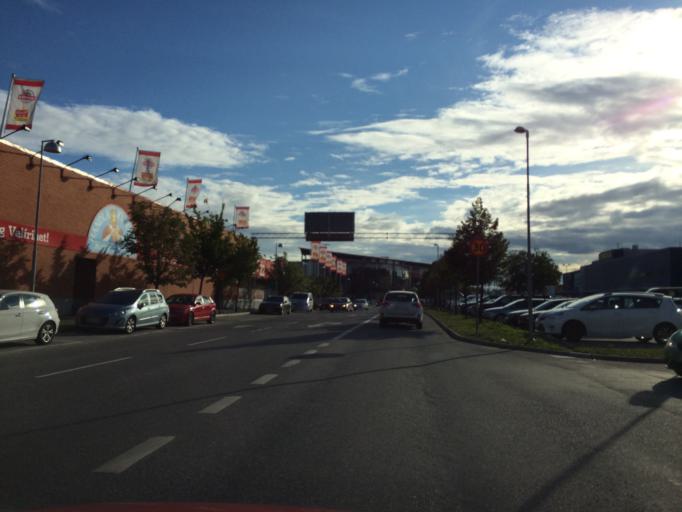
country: SE
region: Stockholm
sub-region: Huddinge Kommun
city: Segeltorp
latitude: 59.2715
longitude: 17.9209
